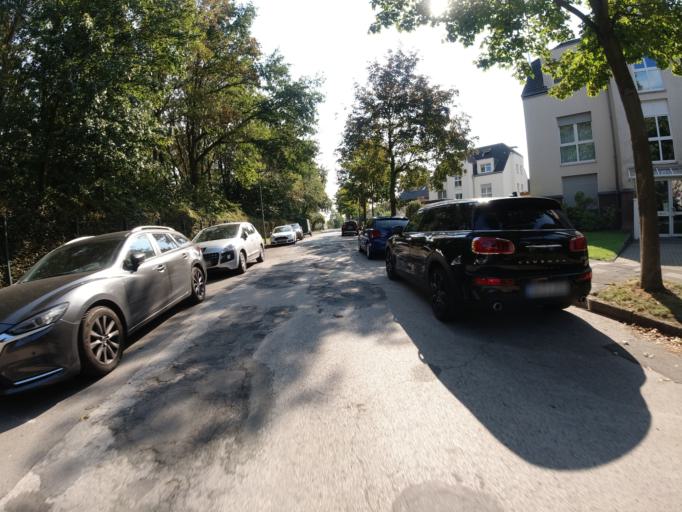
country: DE
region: North Rhine-Westphalia
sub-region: Regierungsbezirk Dusseldorf
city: Hochfeld
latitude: 51.4054
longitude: 6.6923
